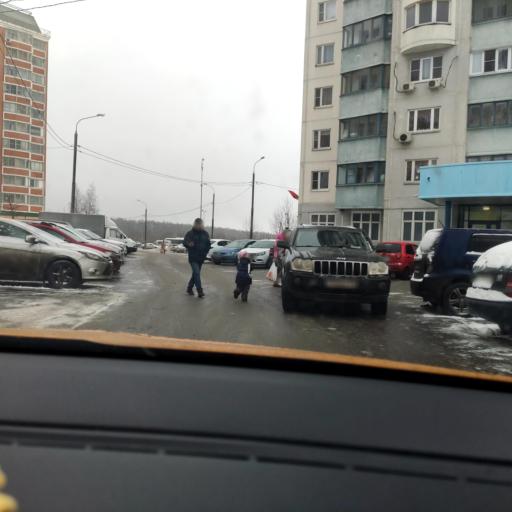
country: RU
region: Moscow
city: Nekrasovka
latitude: 55.7224
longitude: 37.9093
